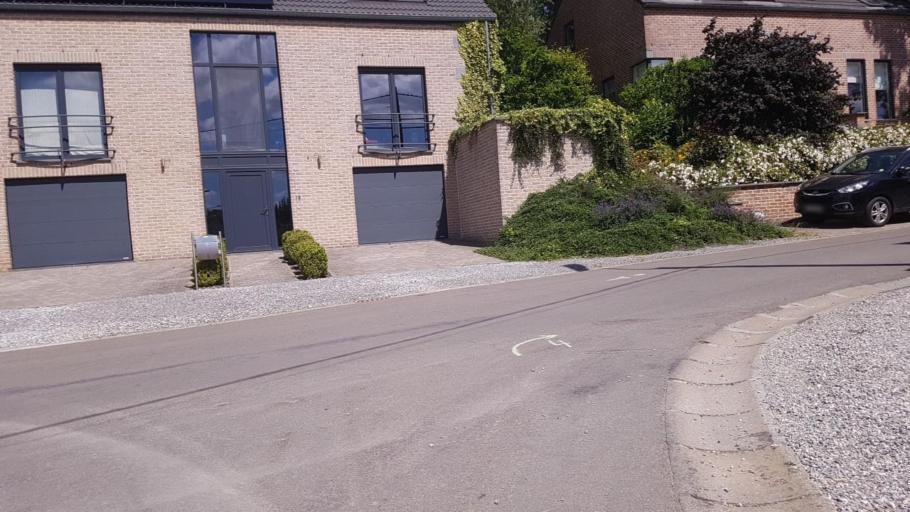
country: BE
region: Wallonia
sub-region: Province du Hainaut
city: Thuin
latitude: 50.3226
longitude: 4.3699
